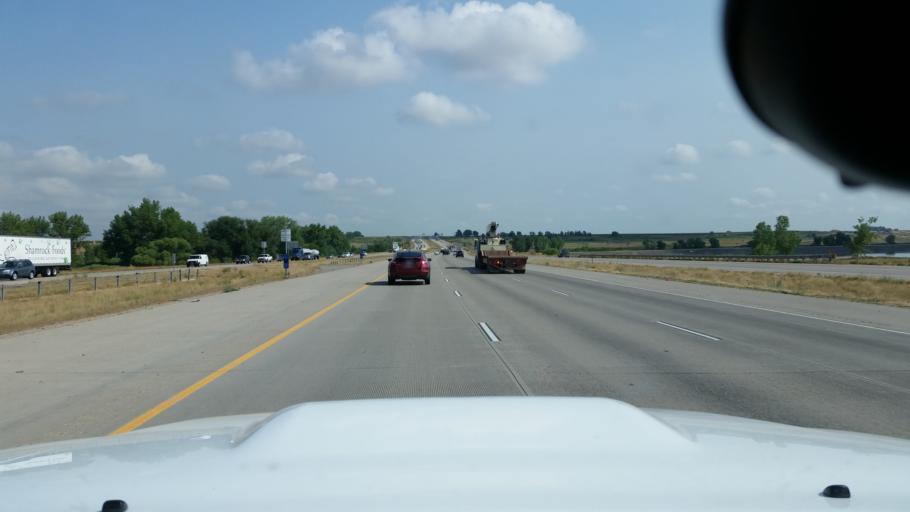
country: US
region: Colorado
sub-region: Weld County
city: Mead
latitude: 40.1689
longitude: -104.9796
